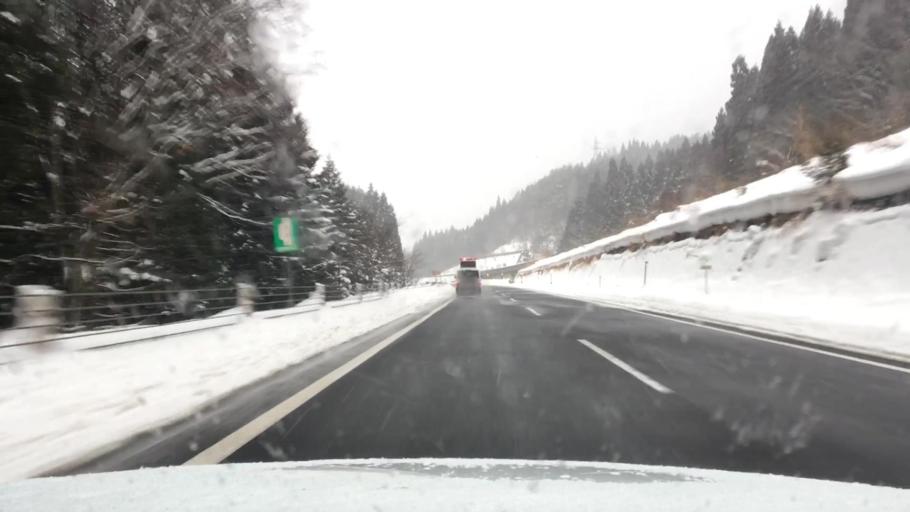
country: JP
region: Akita
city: Hanawa
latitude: 40.1437
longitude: 140.8084
